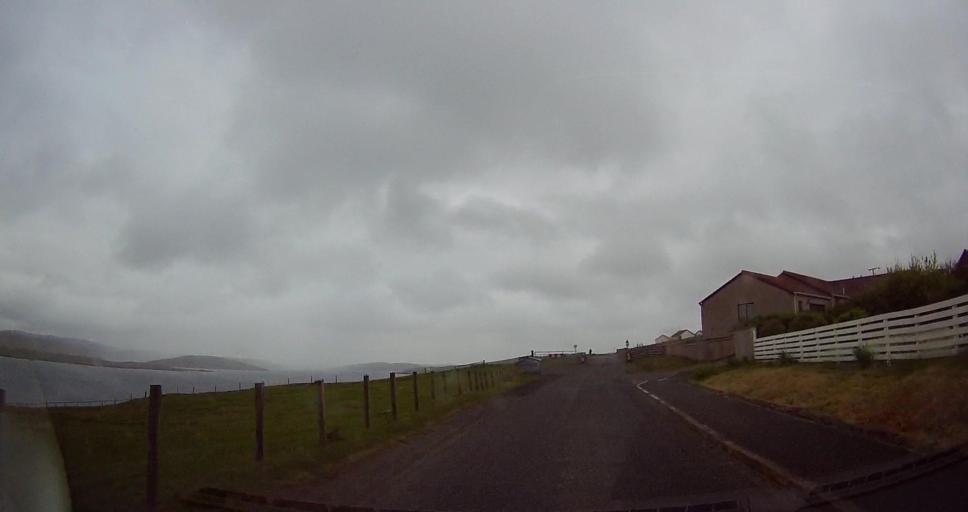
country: GB
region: Scotland
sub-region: Shetland Islands
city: Lerwick
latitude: 60.3896
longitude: -1.3700
